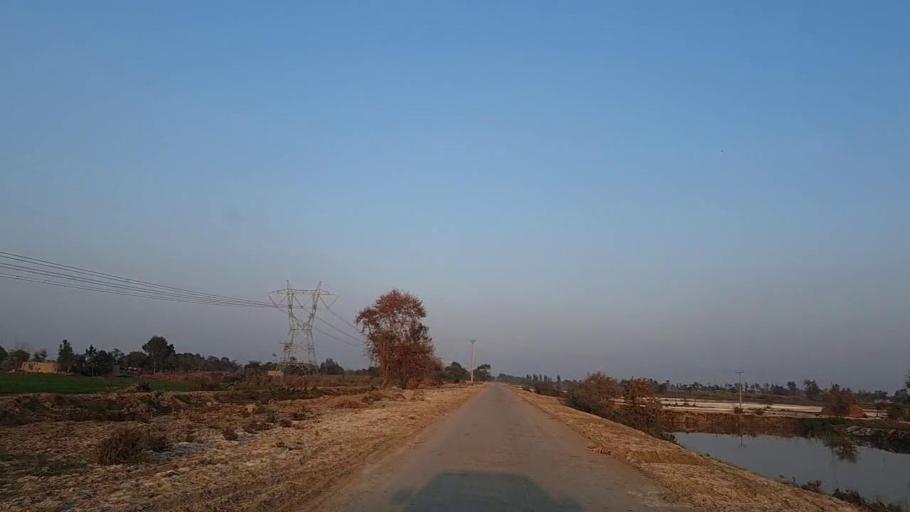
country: PK
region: Sindh
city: Naushahro Firoz
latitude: 26.7669
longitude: 68.0482
